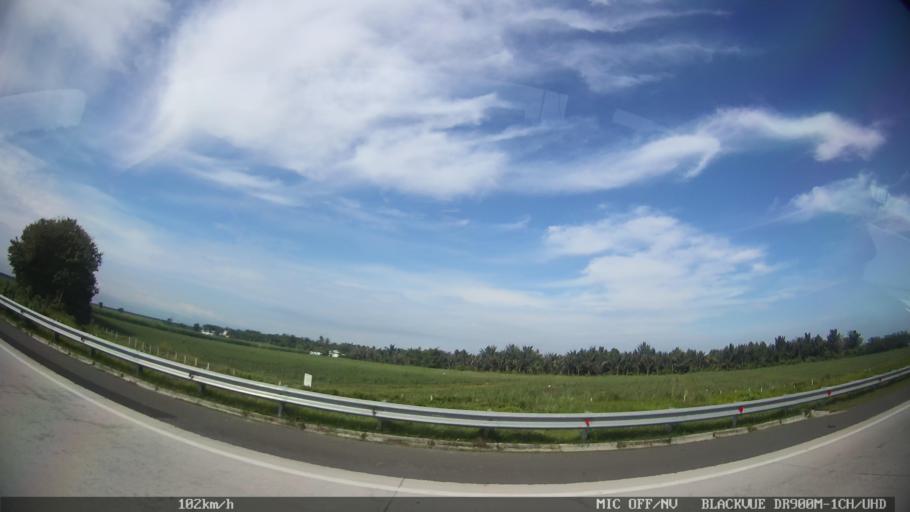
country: ID
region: North Sumatra
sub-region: Kabupaten Langkat
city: Stabat
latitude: 3.7022
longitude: 98.5392
